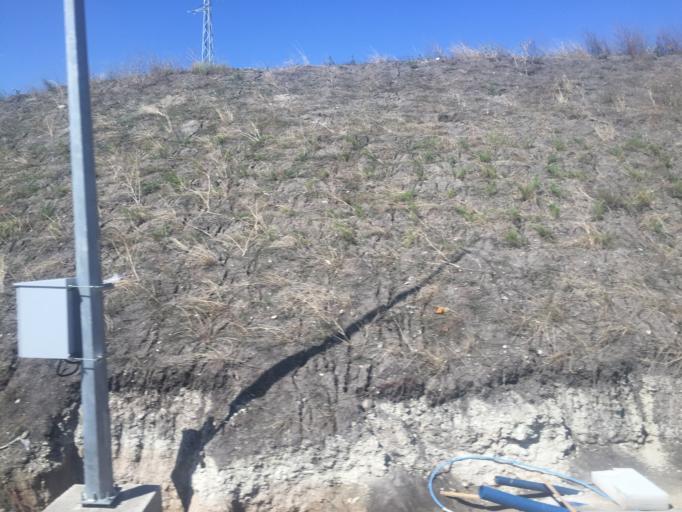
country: TR
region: Balikesir
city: Susurluk
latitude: 39.9627
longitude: 28.1645
